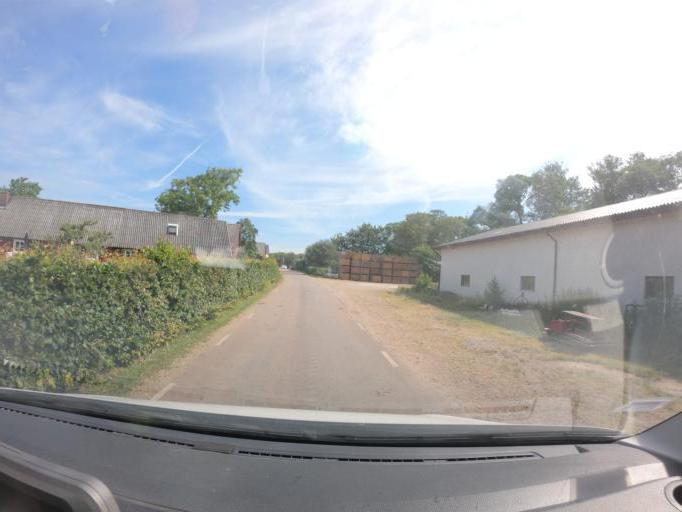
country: SE
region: Skane
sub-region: Angelholms Kommun
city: Vejbystrand
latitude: 56.3957
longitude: 12.6519
